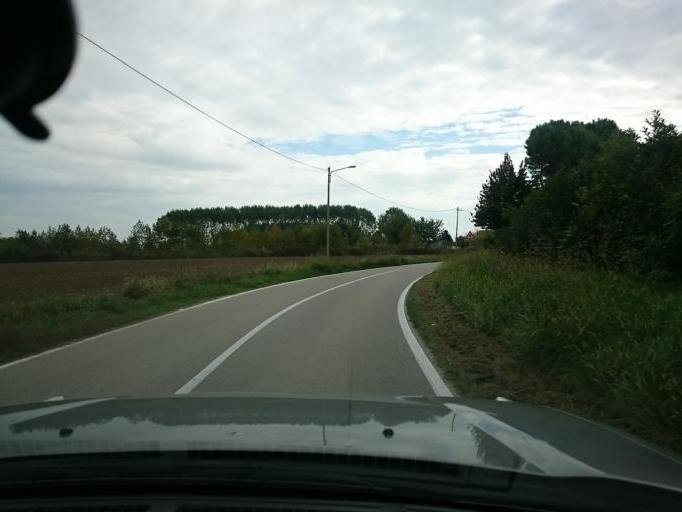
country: IT
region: Veneto
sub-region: Provincia di Padova
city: Ponte San Nicolo
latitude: 45.3725
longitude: 11.9265
